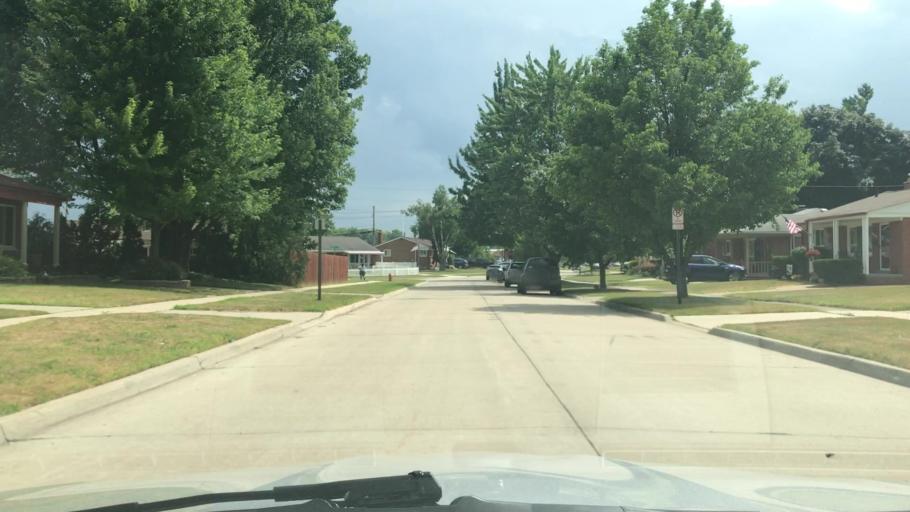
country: US
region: Michigan
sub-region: Oakland County
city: Madison Heights
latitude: 42.5065
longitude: -83.1222
